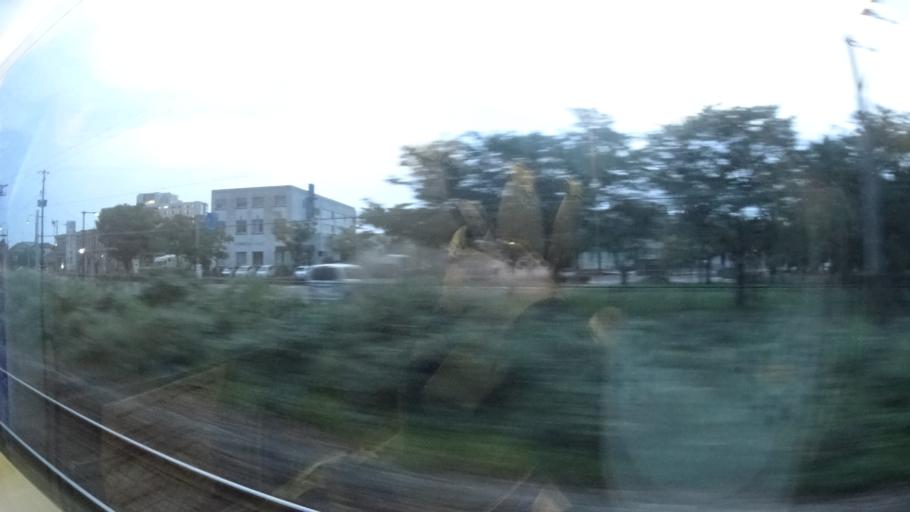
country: JP
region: Niigata
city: Shibata
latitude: 37.9483
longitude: 139.3391
